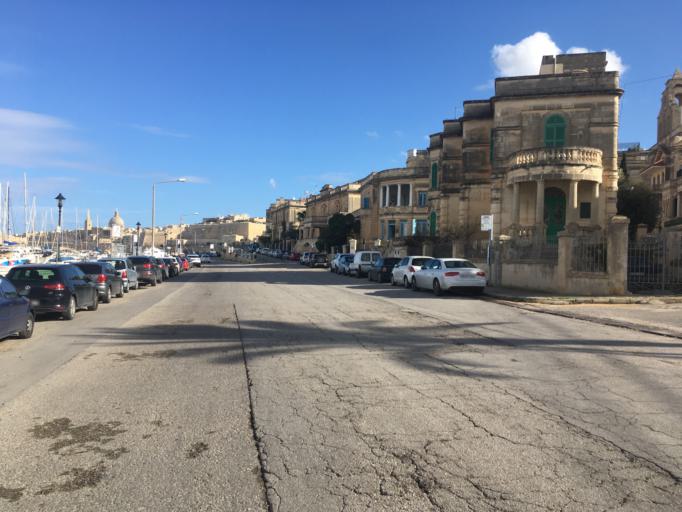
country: MT
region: Ta' Xbiex
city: Ta' Xbiex
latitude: 35.9008
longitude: 14.4976
